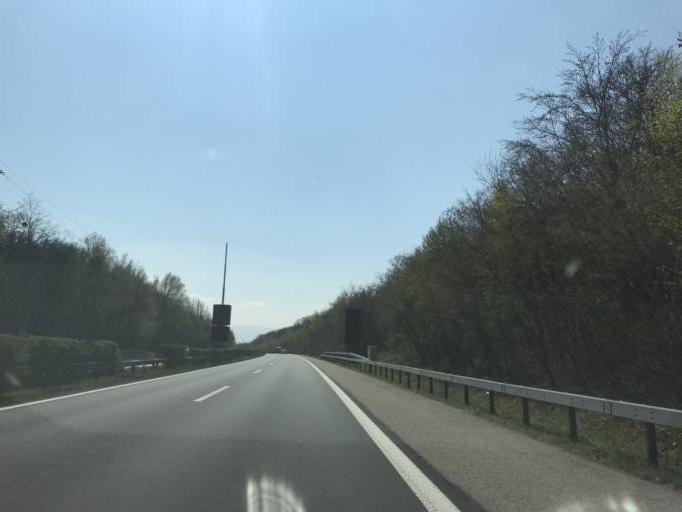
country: FR
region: Rhone-Alpes
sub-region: Departement de l'Ain
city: Sauverny
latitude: 46.3094
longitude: 6.1435
